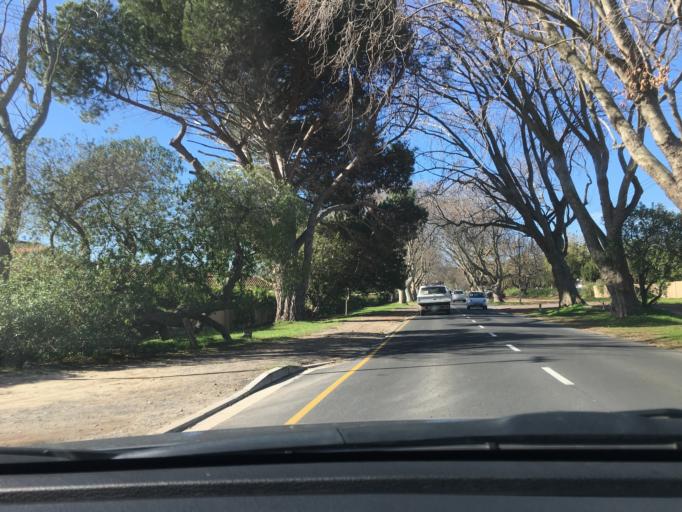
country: ZA
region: Western Cape
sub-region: City of Cape Town
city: Constantia
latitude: -34.0209
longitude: 18.4413
